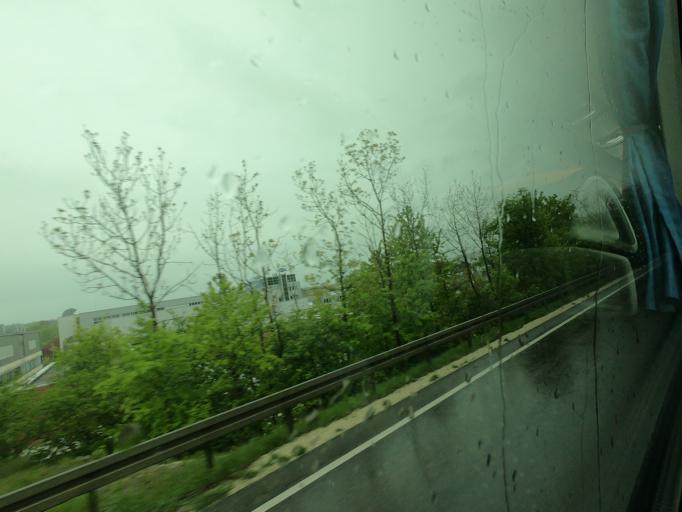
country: DE
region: Baden-Wuerttemberg
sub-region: Regierungsbezirk Stuttgart
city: Aalen
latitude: 48.8304
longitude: 10.0889
